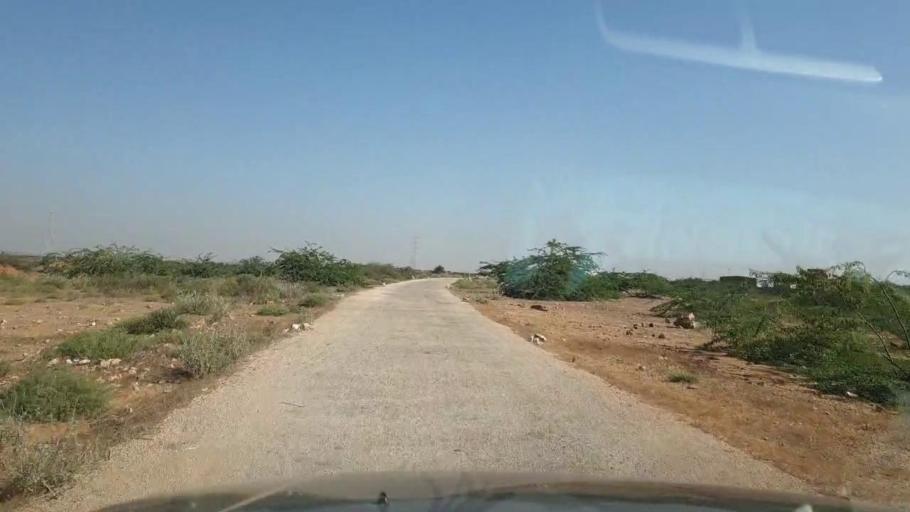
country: PK
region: Sindh
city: Thatta
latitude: 24.8644
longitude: 67.7809
